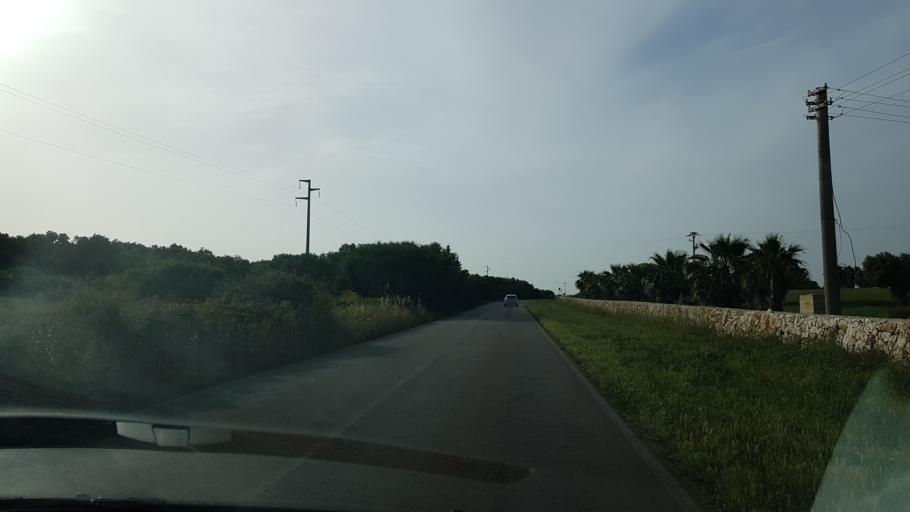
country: IT
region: Apulia
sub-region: Provincia di Lecce
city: Porto Cesareo
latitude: 40.3243
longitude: 17.8547
